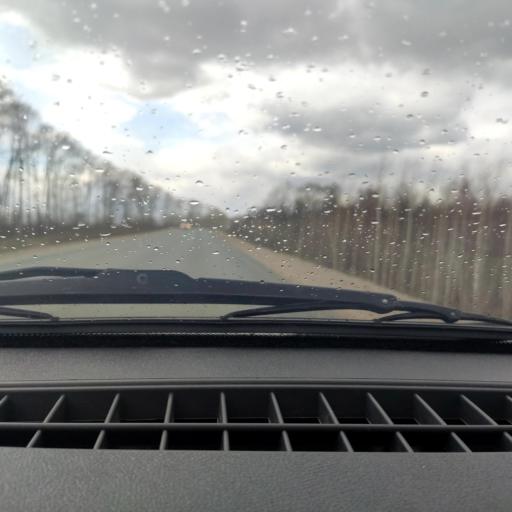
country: RU
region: Bashkortostan
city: Kushnarenkovo
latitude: 55.0603
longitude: 55.1946
